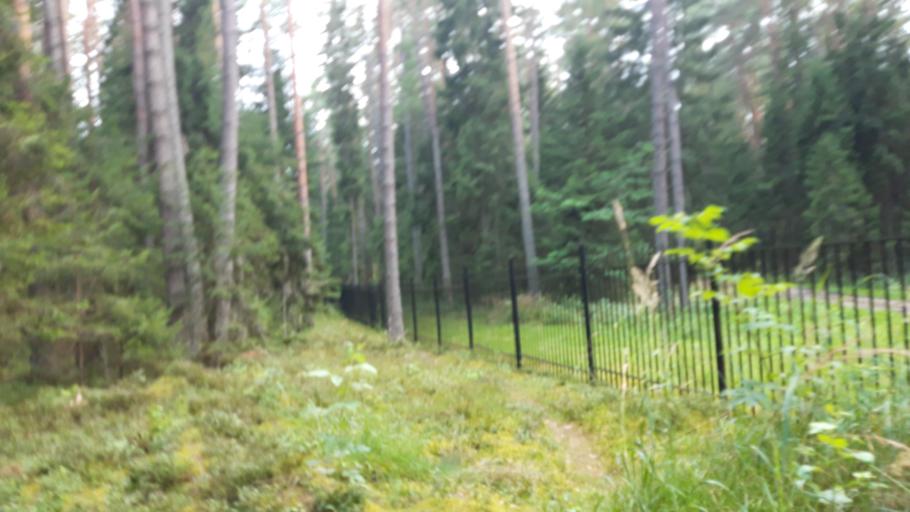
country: RU
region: Tverskaya
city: Konakovo
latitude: 56.6936
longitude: 36.7215
